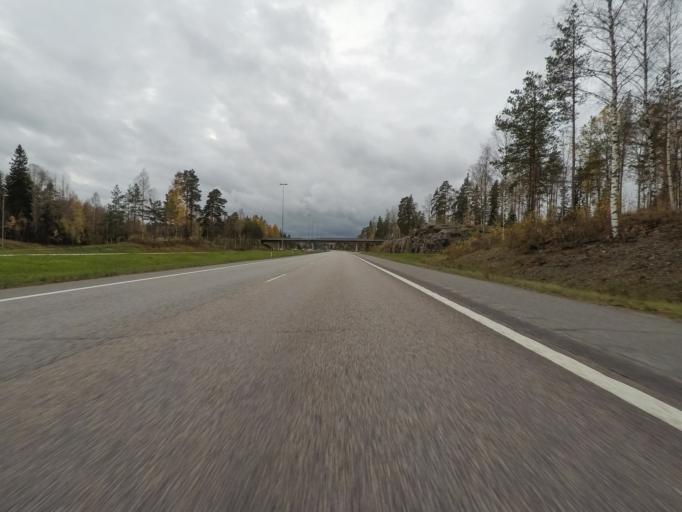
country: FI
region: Uusimaa
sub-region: Porvoo
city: Porvoo
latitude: 60.3729
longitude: 25.5703
